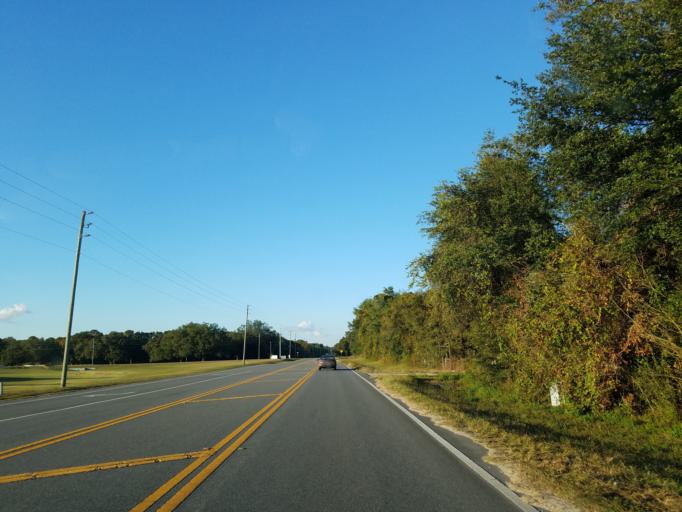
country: US
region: Florida
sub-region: Sumter County
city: Bushnell
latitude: 28.6183
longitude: -82.2034
